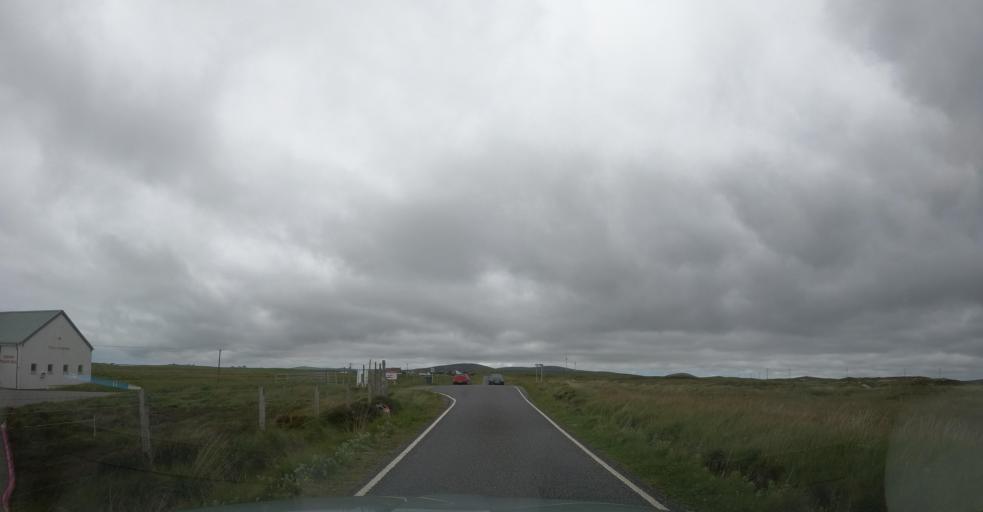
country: GB
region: Scotland
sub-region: Eilean Siar
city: Isle of North Uist
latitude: 57.5455
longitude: -7.3262
